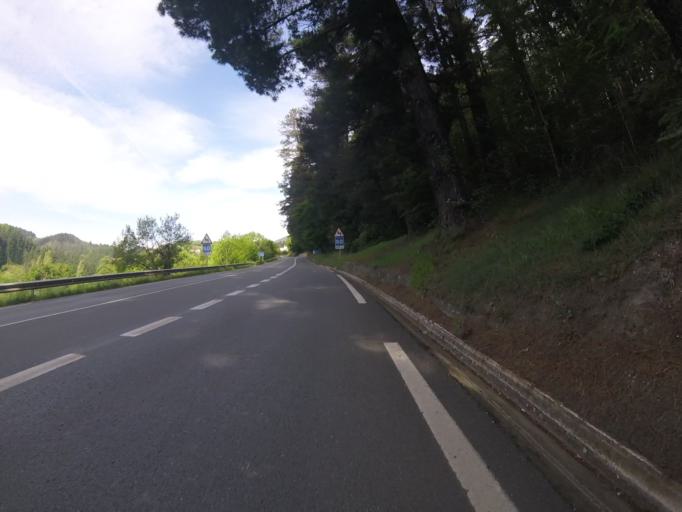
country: ES
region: Basque Country
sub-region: Provincia de Guipuzcoa
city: Zumarraga
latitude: 43.0819
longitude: -2.2997
